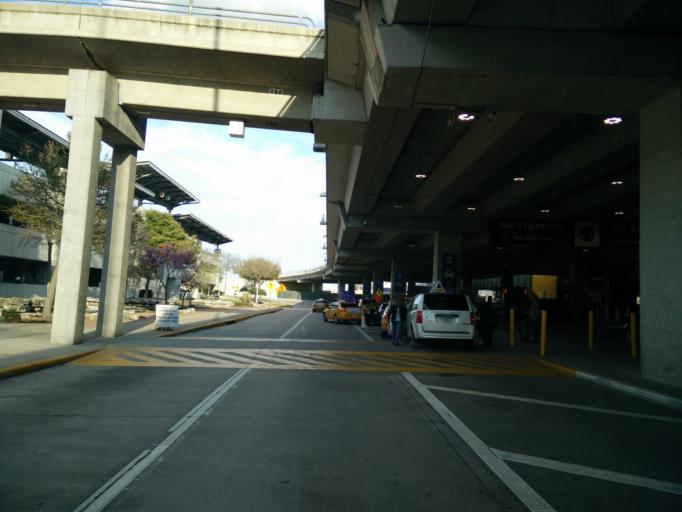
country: US
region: Texas
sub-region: Travis County
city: Hornsby Bend
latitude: 30.2029
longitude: -97.6668
